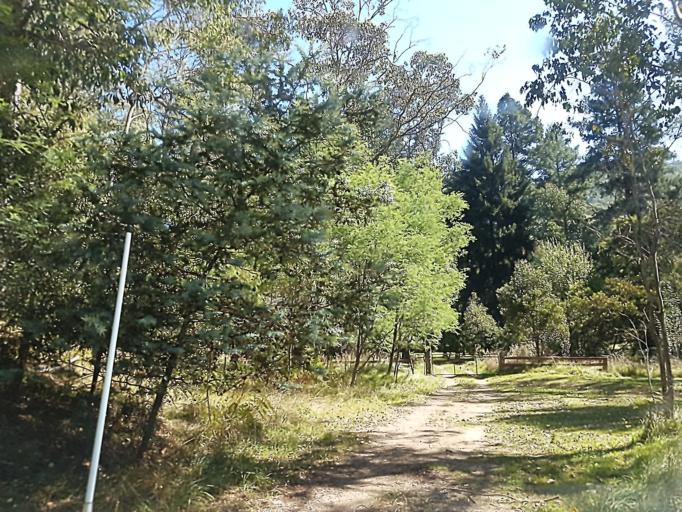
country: AU
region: Victoria
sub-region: Alpine
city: Mount Beauty
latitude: -36.8216
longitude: 147.0627
